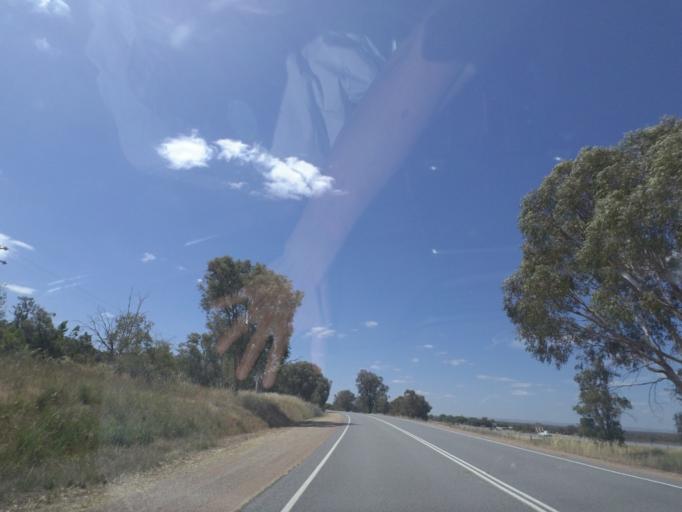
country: AU
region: Victoria
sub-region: Wangaratta
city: Wangaratta
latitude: -36.4581
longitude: 146.2359
